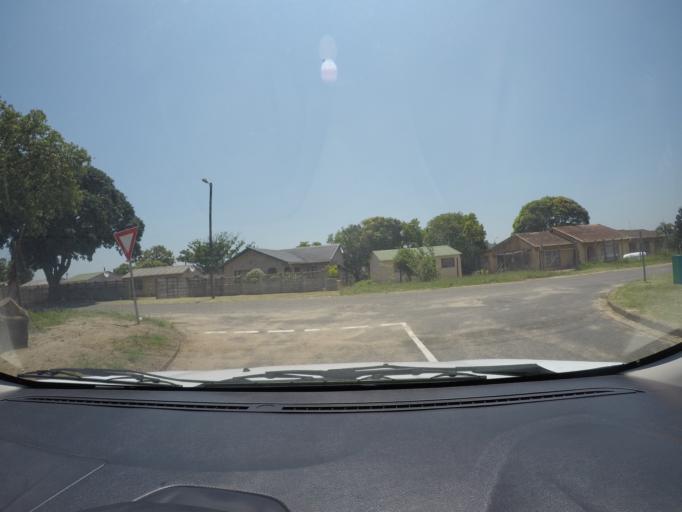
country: ZA
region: KwaZulu-Natal
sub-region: uThungulu District Municipality
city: eSikhawini
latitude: -28.8803
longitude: 31.8939
